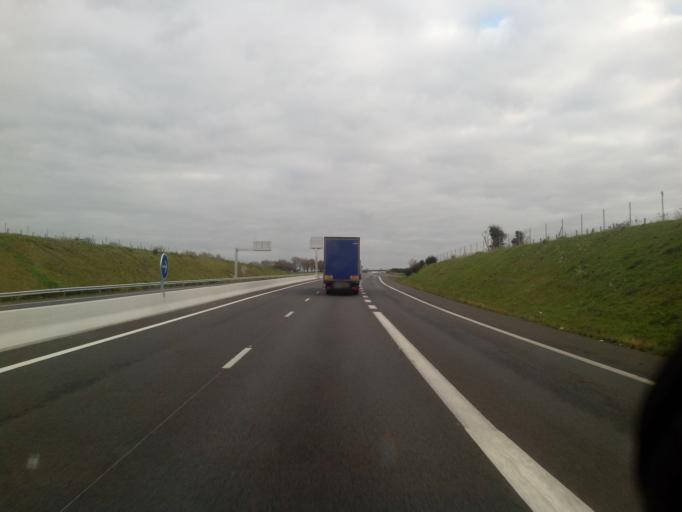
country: FR
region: Poitou-Charentes
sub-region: Departement des Deux-Sevres
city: Le Pin
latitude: 46.8967
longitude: -0.6276
